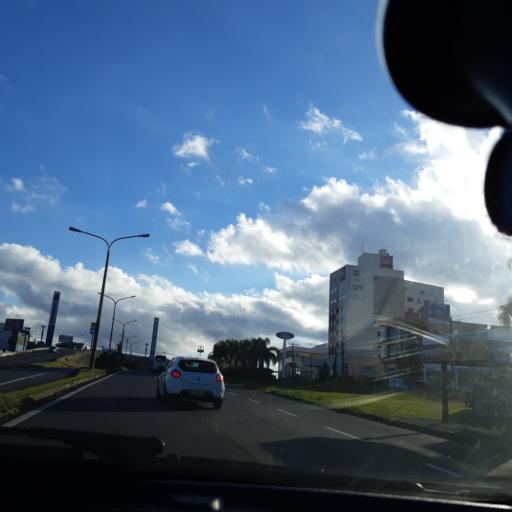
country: BR
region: Rio Grande do Sul
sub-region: Caxias Do Sul
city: Caxias do Sul
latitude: -29.1754
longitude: -51.2138
